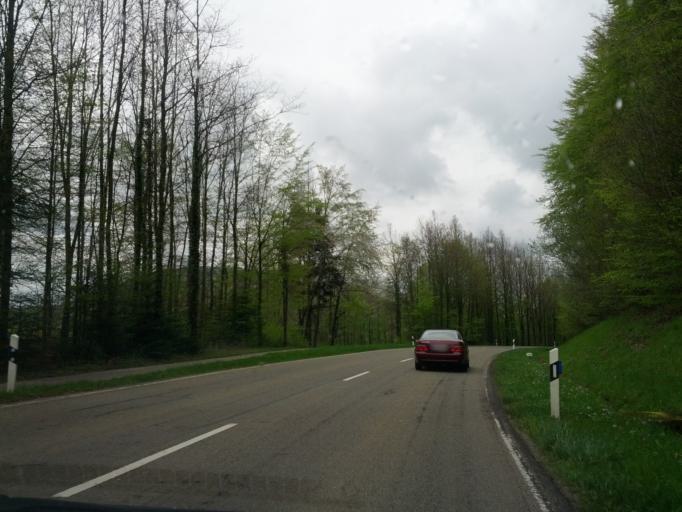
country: DE
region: Baden-Wuerttemberg
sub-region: Freiburg Region
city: Solden
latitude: 47.9256
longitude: 7.8047
